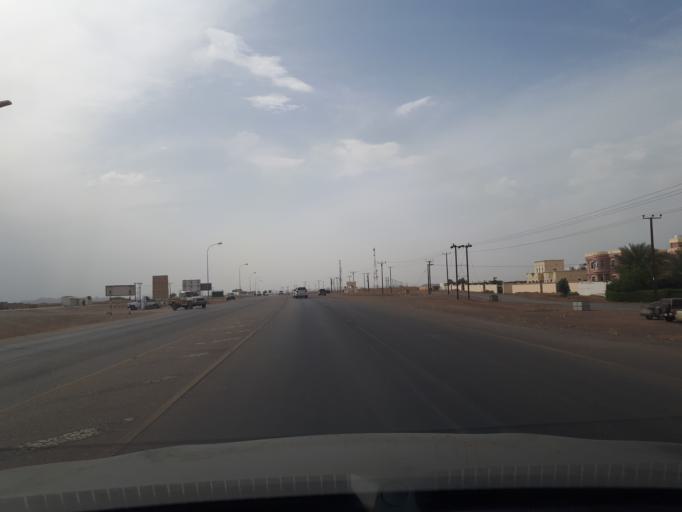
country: OM
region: Ash Sharqiyah
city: Badiyah
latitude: 22.5048
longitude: 58.7468
